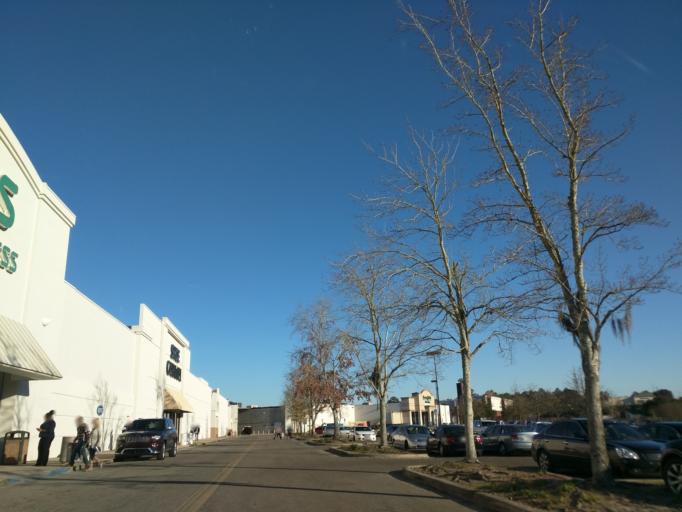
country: US
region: Florida
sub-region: Leon County
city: Tallahassee
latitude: 30.4762
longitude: -84.2937
